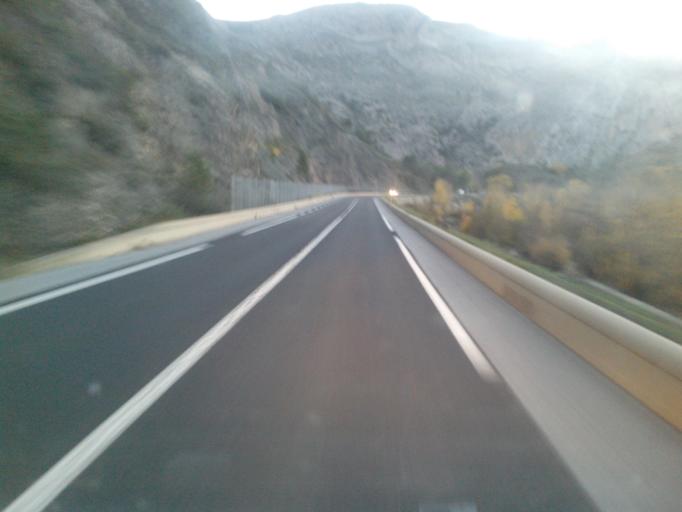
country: FR
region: Languedoc-Roussillon
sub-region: Departement des Pyrenees-Orientales
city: Baixas
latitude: 42.7743
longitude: 2.7872
